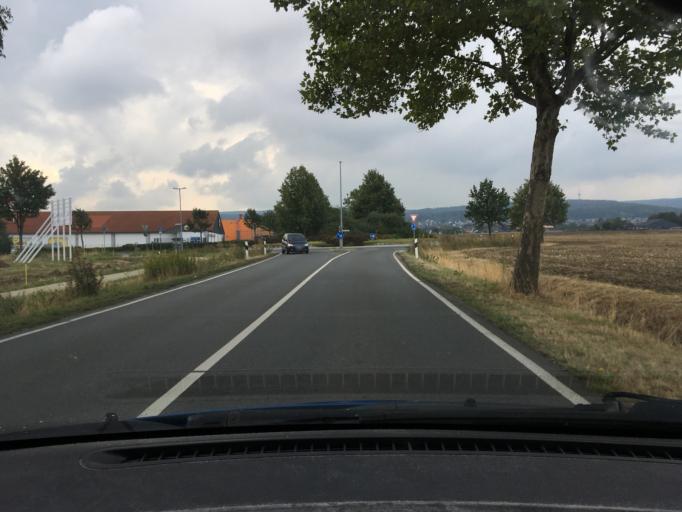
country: DE
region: Lower Saxony
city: Barsinghausen
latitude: 52.3177
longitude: 9.4647
